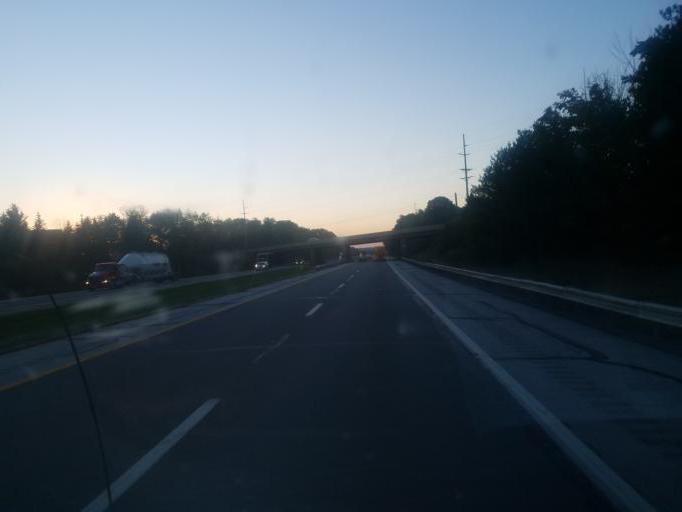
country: US
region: Ohio
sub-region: Mahoning County
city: Canfield
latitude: 41.0255
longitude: -80.7245
